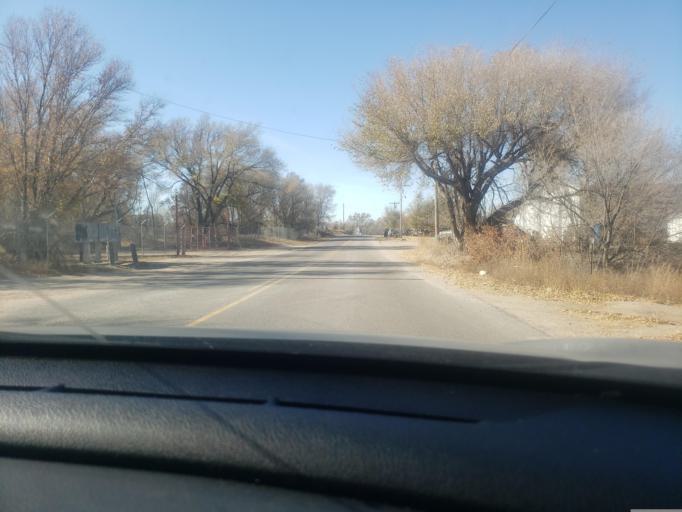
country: US
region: Kansas
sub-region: Finney County
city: Garden City
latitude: 37.9511
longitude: -100.8705
